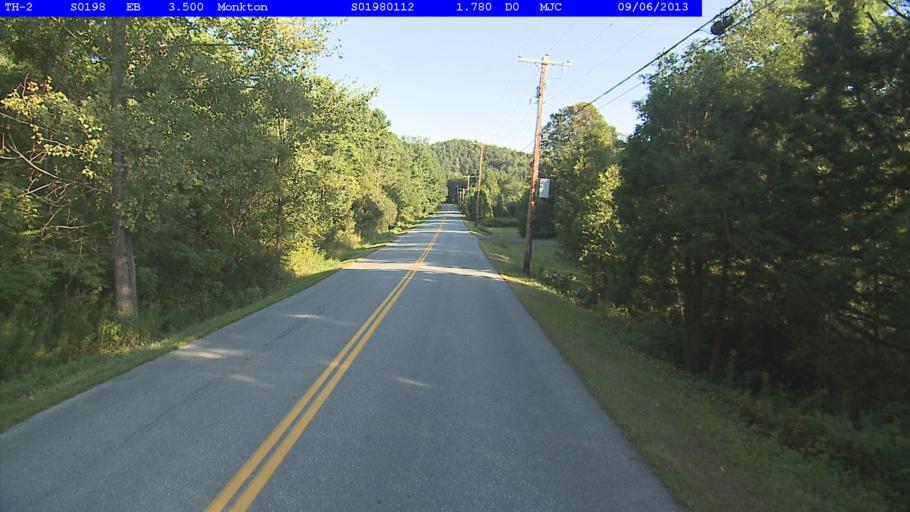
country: US
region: Vermont
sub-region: Chittenden County
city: Hinesburg
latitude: 44.2449
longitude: -73.1653
